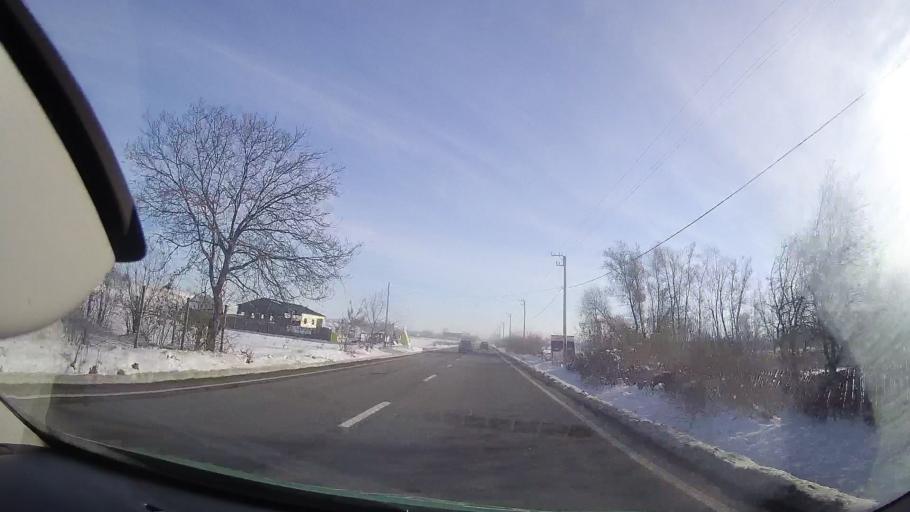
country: RO
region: Neamt
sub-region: Comuna Ghindaoani
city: Ghindaoani
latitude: 47.0828
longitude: 26.3403
